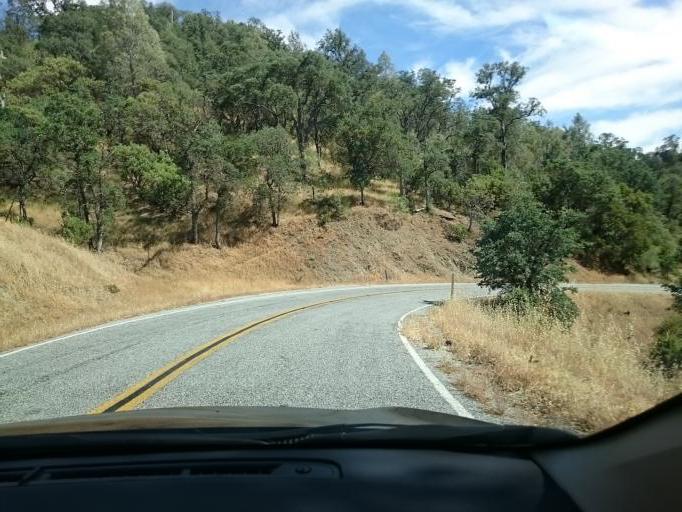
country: US
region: California
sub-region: Santa Clara County
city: East Foothills
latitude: 37.3569
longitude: -121.5839
